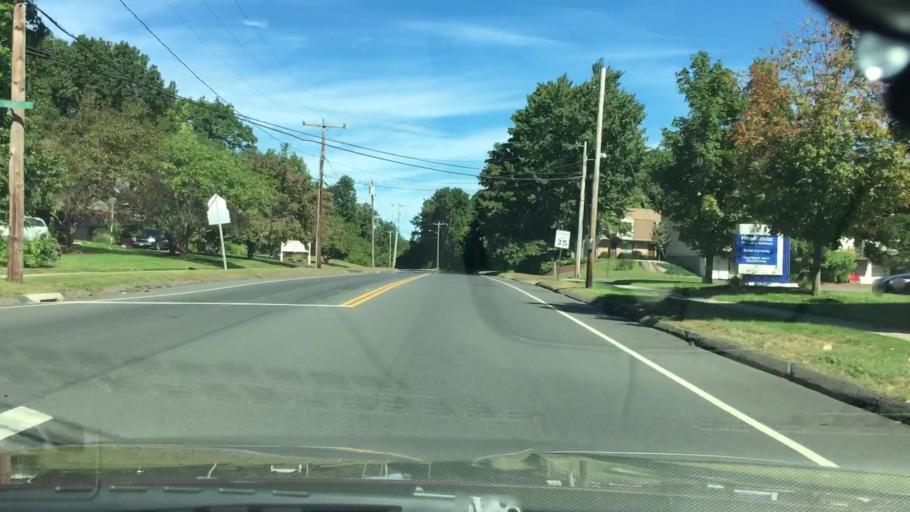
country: US
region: Connecticut
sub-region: Litchfield County
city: Terryville
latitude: 41.6854
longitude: -72.9841
